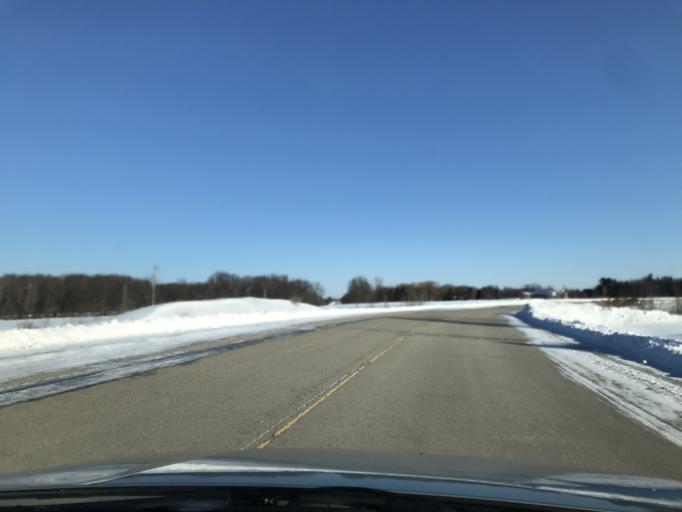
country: US
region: Wisconsin
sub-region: Oconto County
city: Oconto Falls
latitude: 44.9684
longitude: -88.0460
